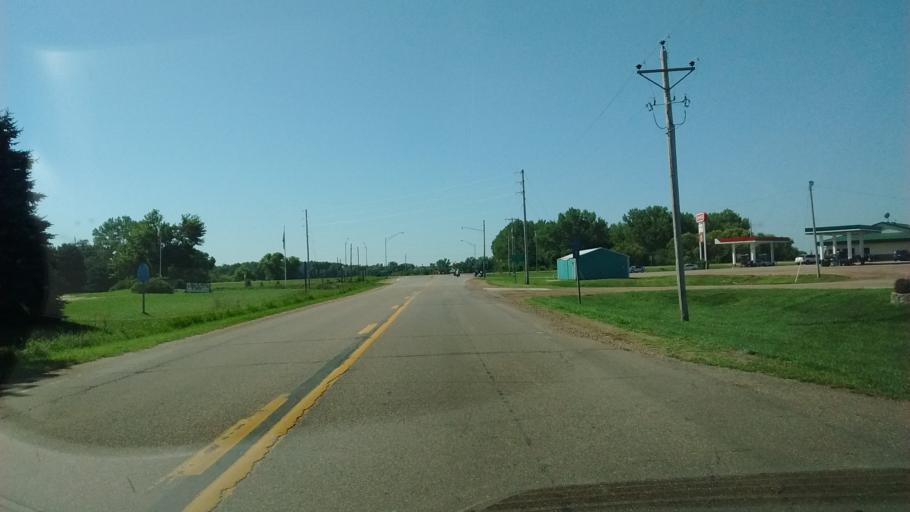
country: US
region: Iowa
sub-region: Woodbury County
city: Moville
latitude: 42.4843
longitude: -96.0758
